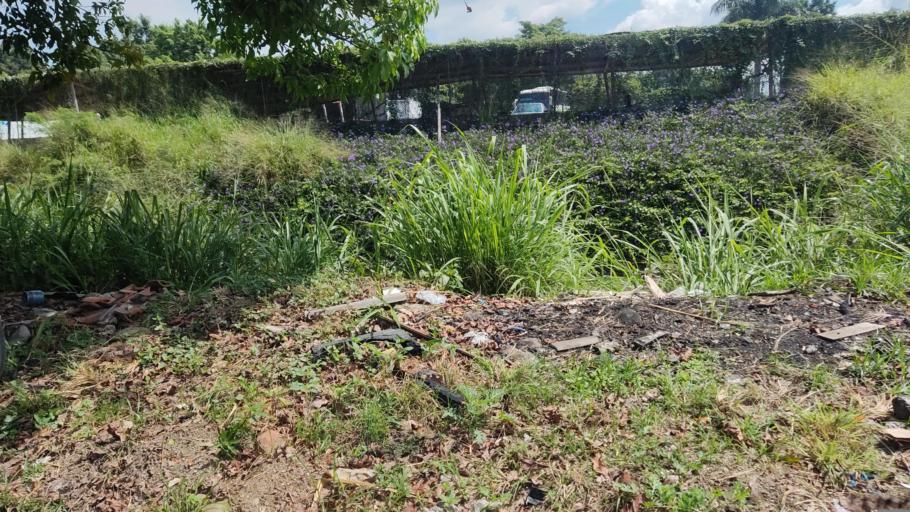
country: CO
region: Valle del Cauca
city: Cali
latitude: 3.4123
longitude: -76.5221
